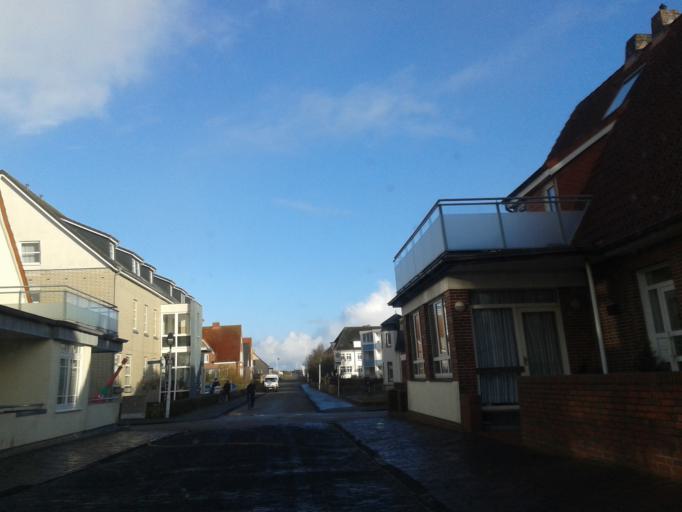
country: DE
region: Lower Saxony
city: Norderney
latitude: 53.7096
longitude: 7.1514
